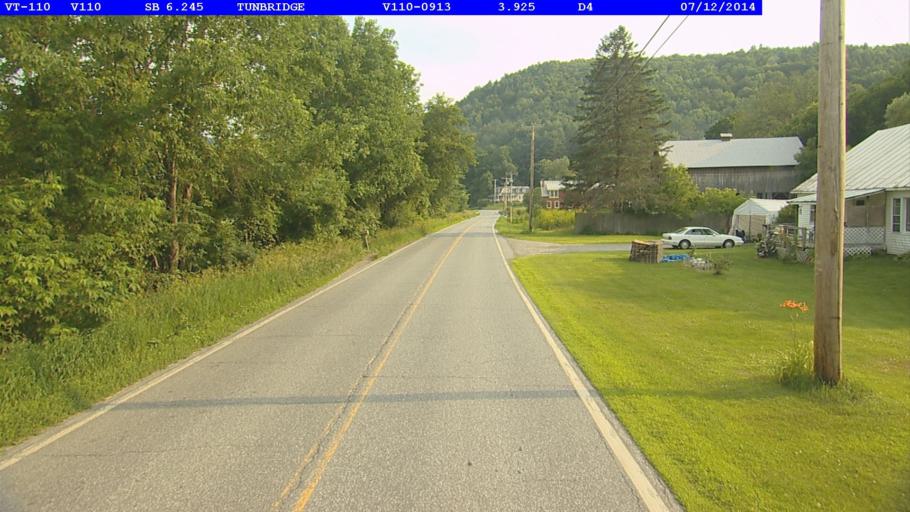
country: US
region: Vermont
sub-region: Orange County
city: Chelsea
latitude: 43.9017
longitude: -72.4857
